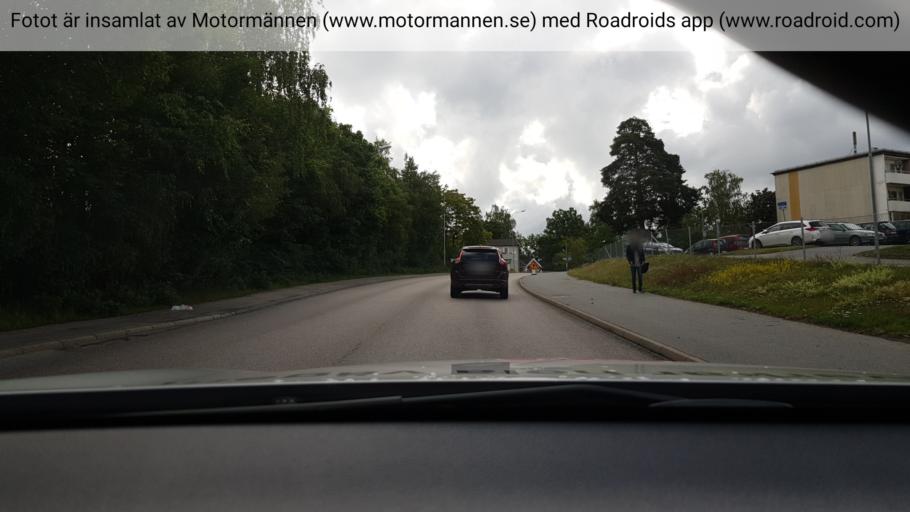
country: SE
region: Stockholm
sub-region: Haninge Kommun
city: Haninge
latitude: 59.1743
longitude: 18.1450
